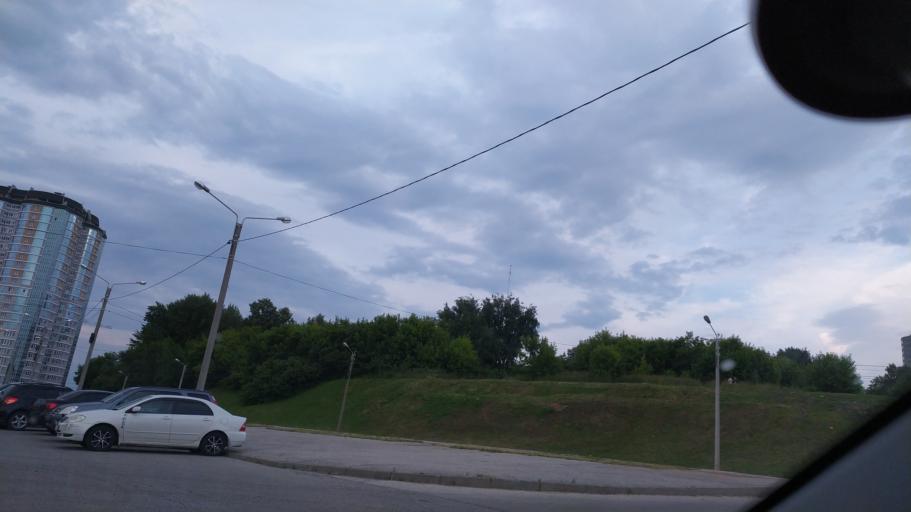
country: RU
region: Chuvashia
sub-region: Cheboksarskiy Rayon
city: Cheboksary
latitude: 56.1472
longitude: 47.2595
